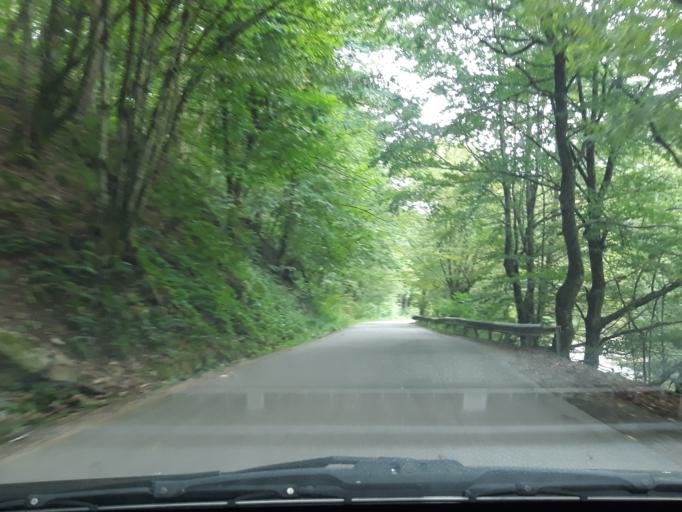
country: RO
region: Bihor
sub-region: Comuna Pietroasa
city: Pietroasa
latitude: 46.5875
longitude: 22.6094
